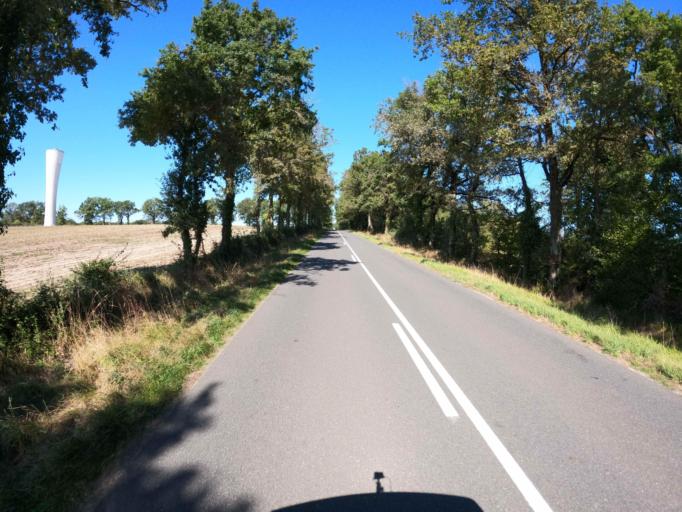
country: FR
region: Poitou-Charentes
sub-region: Departement de la Vienne
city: Lathus-Saint-Remy
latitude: 46.3222
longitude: 0.9706
